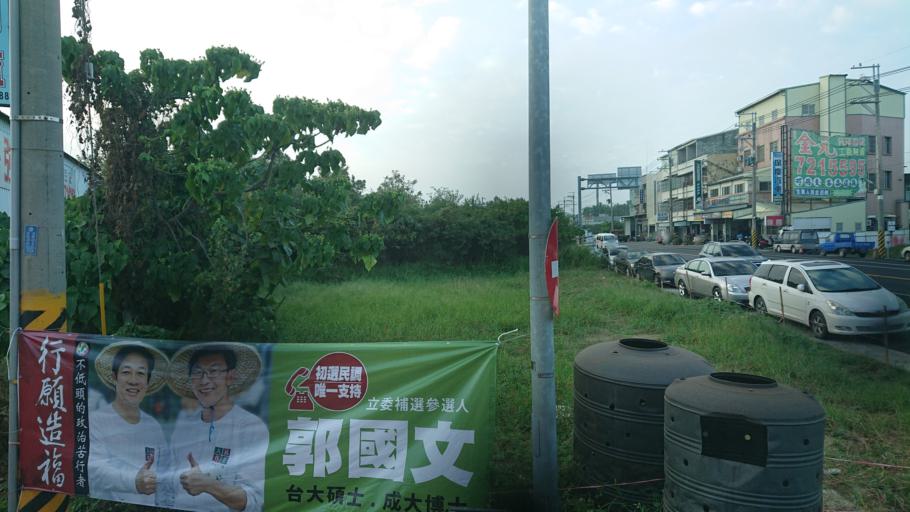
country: TW
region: Taiwan
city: Xinying
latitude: 23.1861
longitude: 120.2396
